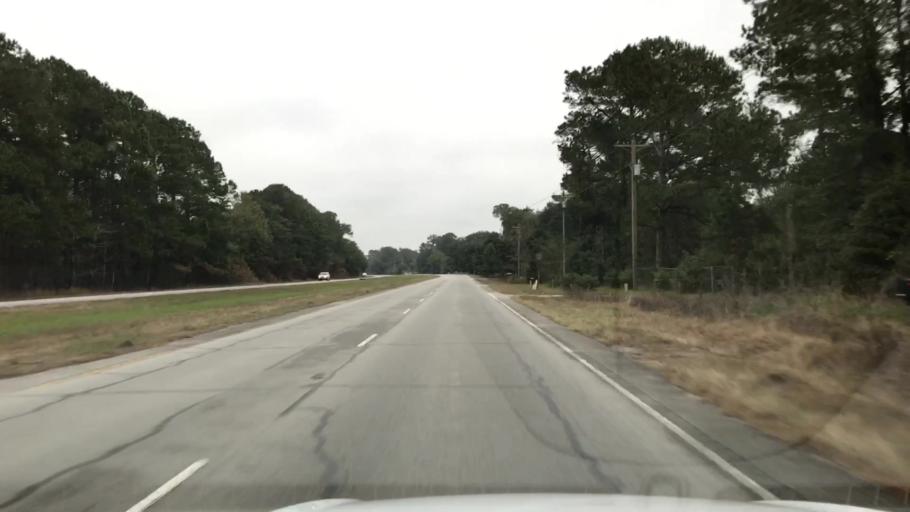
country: US
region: South Carolina
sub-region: Charleston County
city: Awendaw
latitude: 33.0722
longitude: -79.5172
